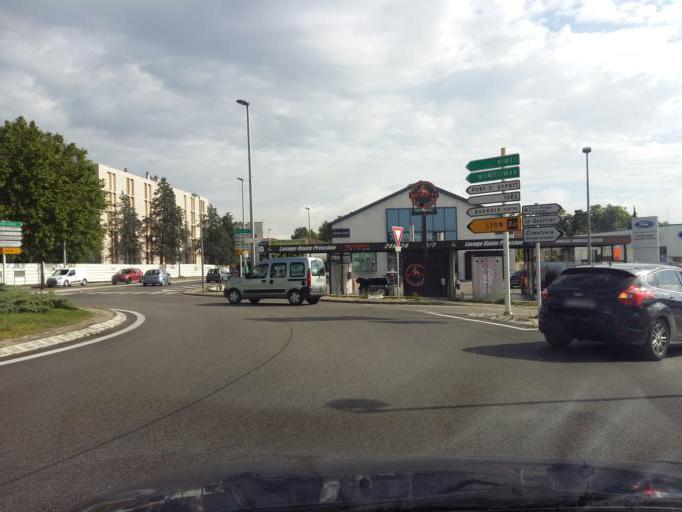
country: FR
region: Languedoc-Roussillon
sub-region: Departement du Gard
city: Bagnols-sur-Ceze
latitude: 44.1598
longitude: 4.6255
